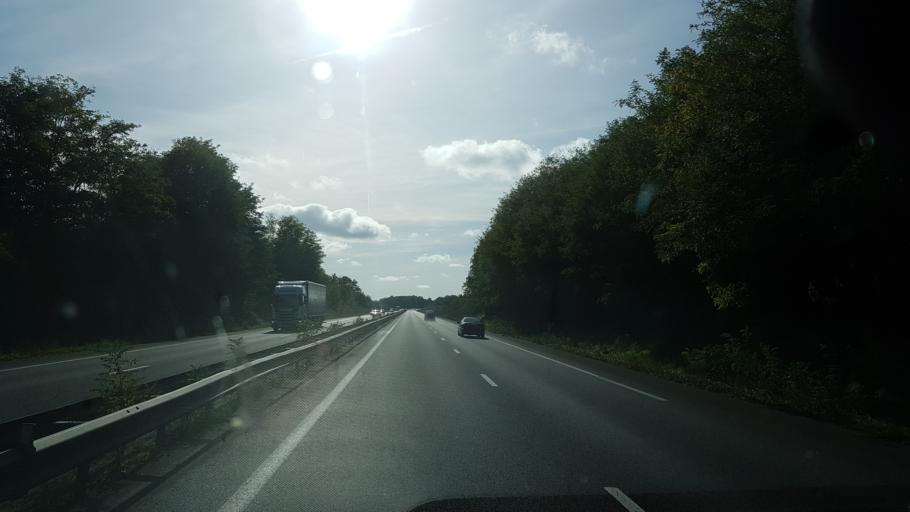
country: FR
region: Poitou-Charentes
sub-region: Departement de la Charente
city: Chasseneuil-sur-Bonnieure
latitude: 45.8018
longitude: 0.4391
